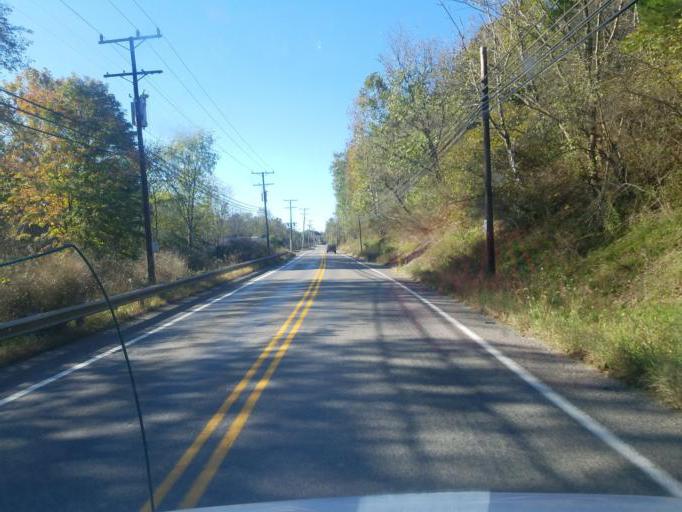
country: US
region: Pennsylvania
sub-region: Allegheny County
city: Imperial
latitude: 40.4596
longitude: -80.2606
